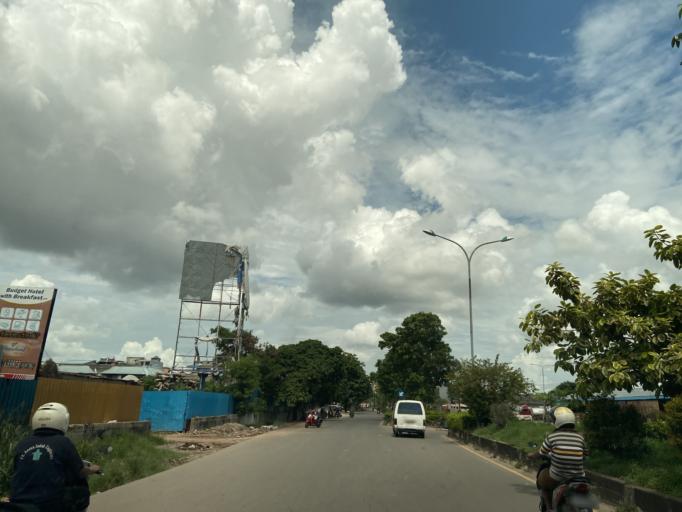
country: SG
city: Singapore
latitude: 1.1462
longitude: 104.0034
